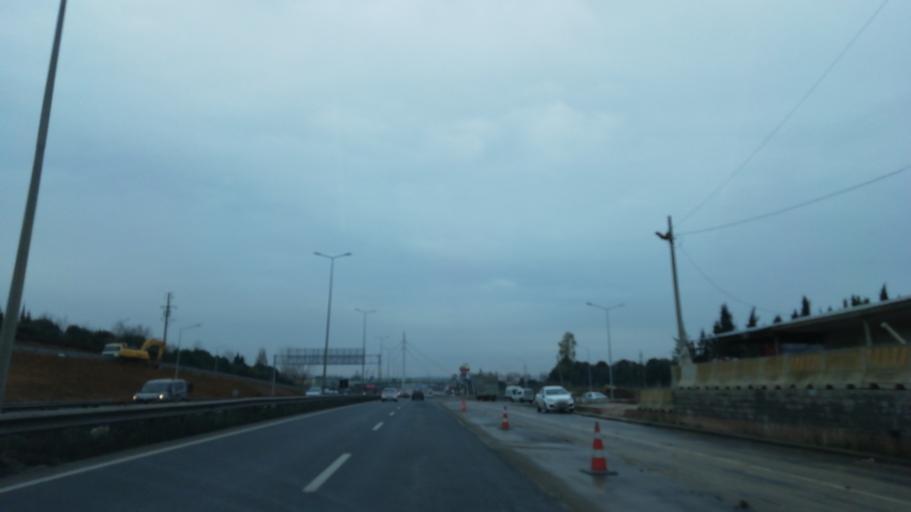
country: TR
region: Kocaeli
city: Darica
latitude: 40.8135
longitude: 29.3659
